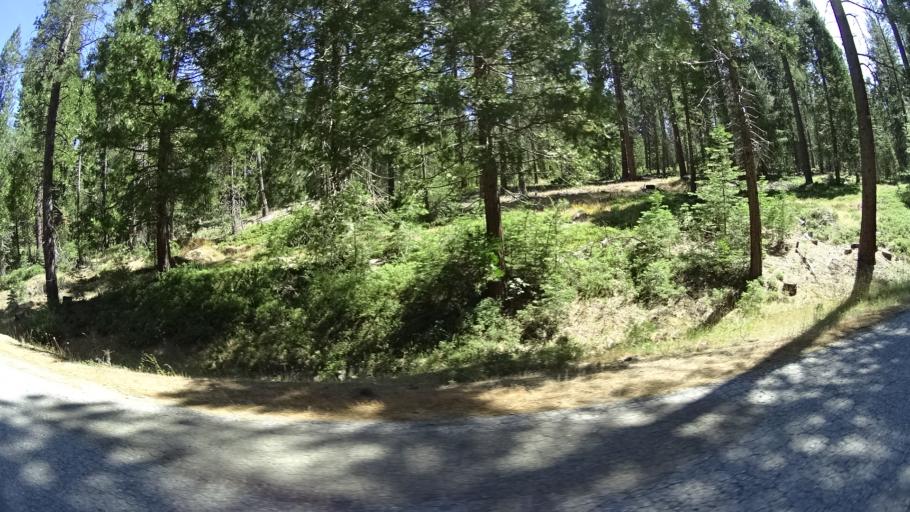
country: US
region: California
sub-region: Amador County
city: Pioneer
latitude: 38.4310
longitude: -120.4582
